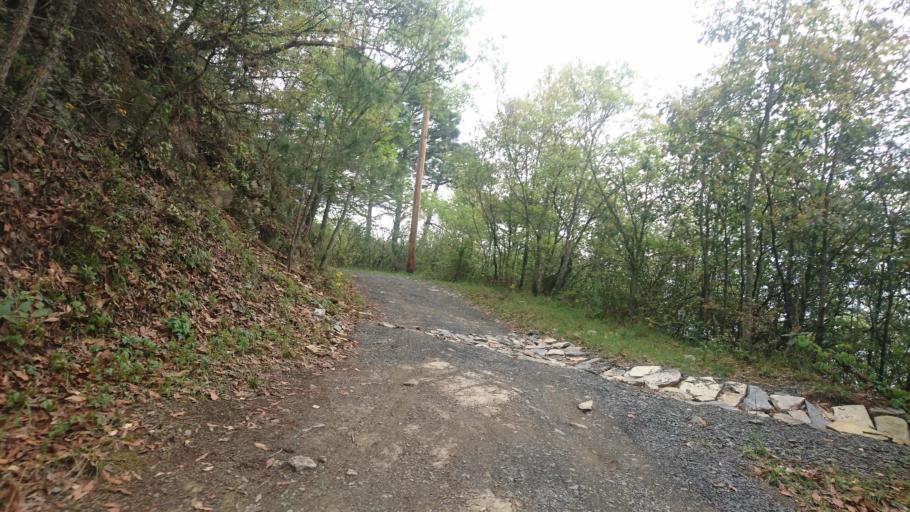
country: MX
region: Nuevo Leon
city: Garza Garcia
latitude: 25.6060
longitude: -100.3435
